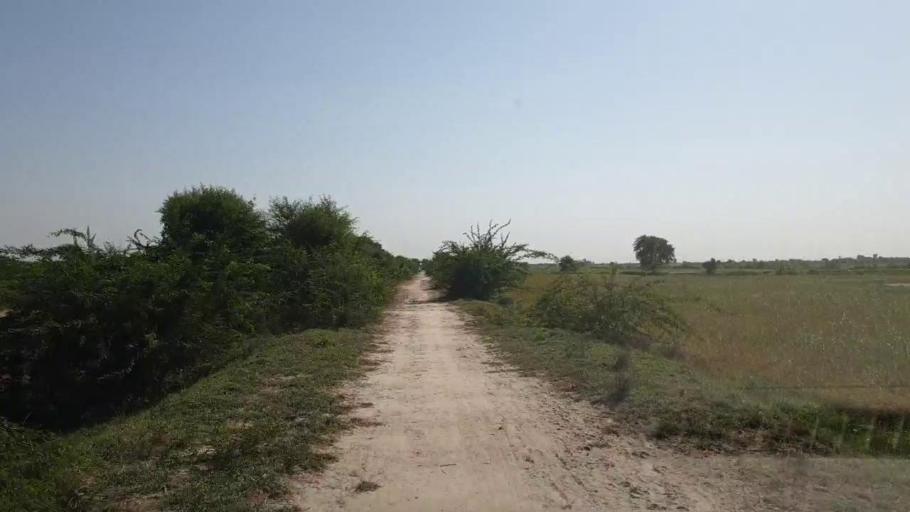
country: PK
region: Sindh
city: Kadhan
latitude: 24.6005
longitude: 69.0045
